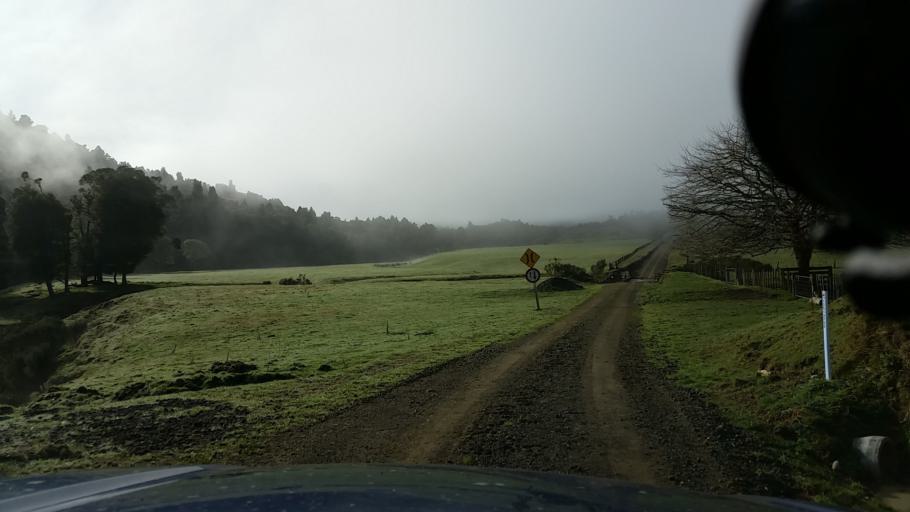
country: NZ
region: Taranaki
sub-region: New Plymouth District
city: Waitara
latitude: -38.9781
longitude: 174.7496
